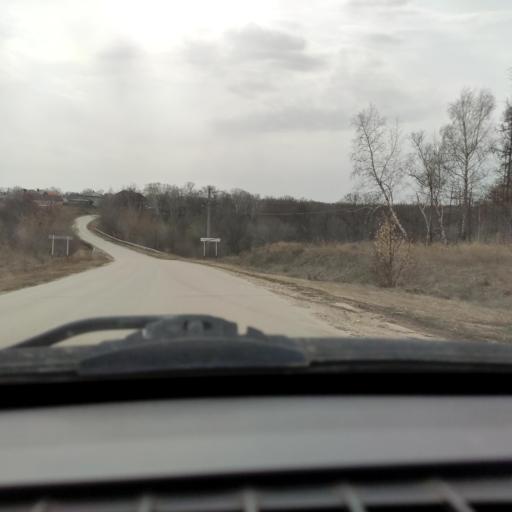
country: RU
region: Samara
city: Dubovyy Umet
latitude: 53.0398
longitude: 50.1738
